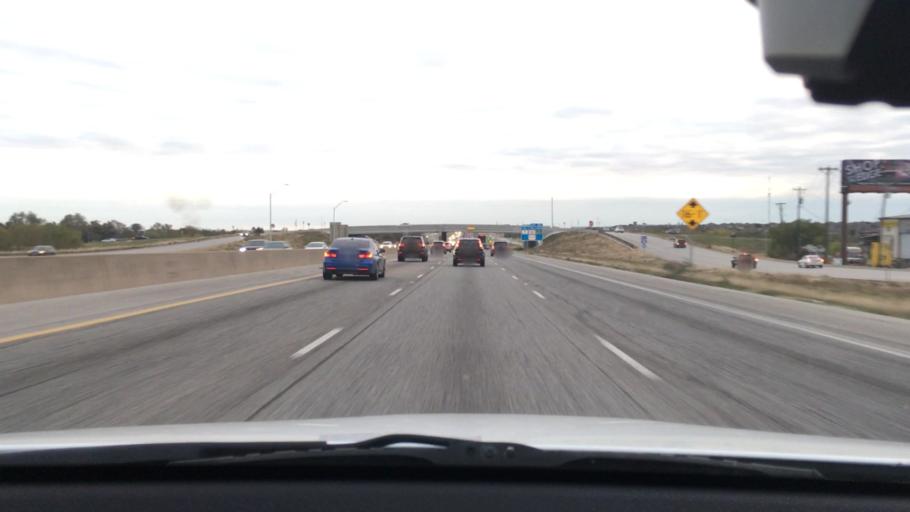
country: US
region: Texas
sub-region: Hays County
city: Buda
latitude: 30.0617
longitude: -97.8331
